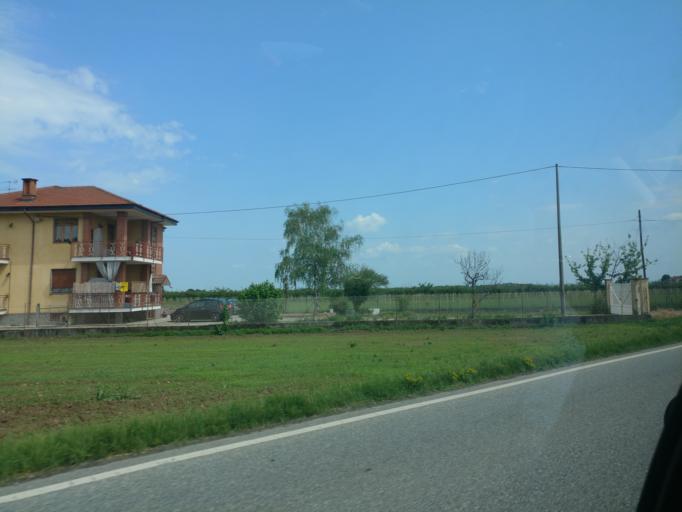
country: IT
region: Piedmont
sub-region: Provincia di Torino
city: Cavour
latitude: 44.7744
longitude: 7.3885
